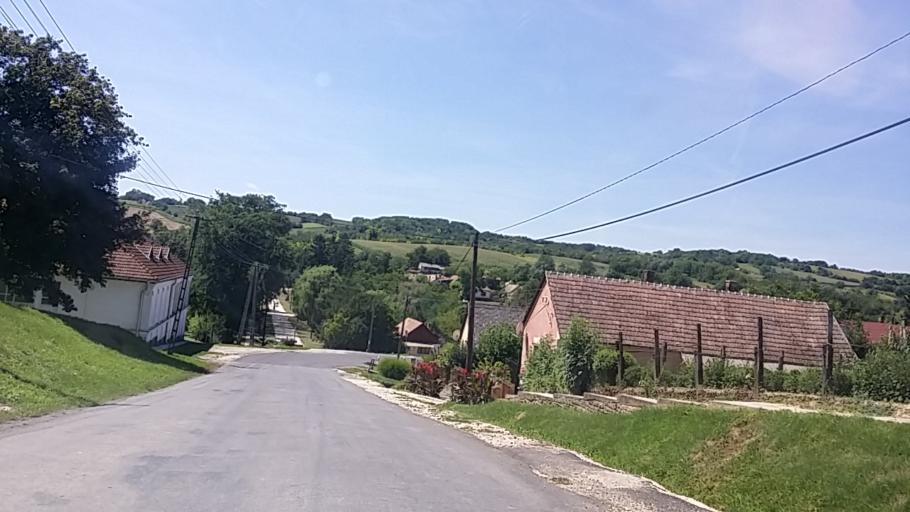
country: HU
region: Somogy
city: Karad
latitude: 46.6926
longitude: 17.8395
